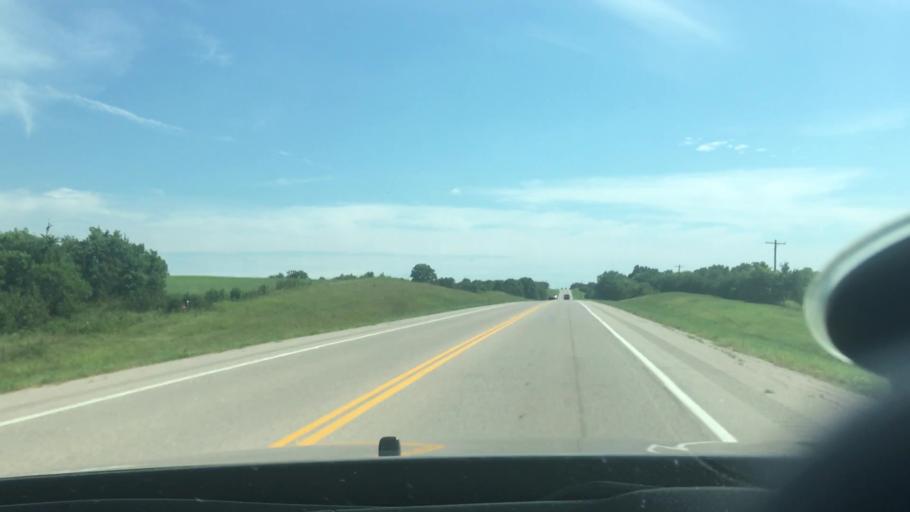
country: US
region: Oklahoma
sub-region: Seminole County
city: Konawa
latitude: 34.9966
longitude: -96.6791
